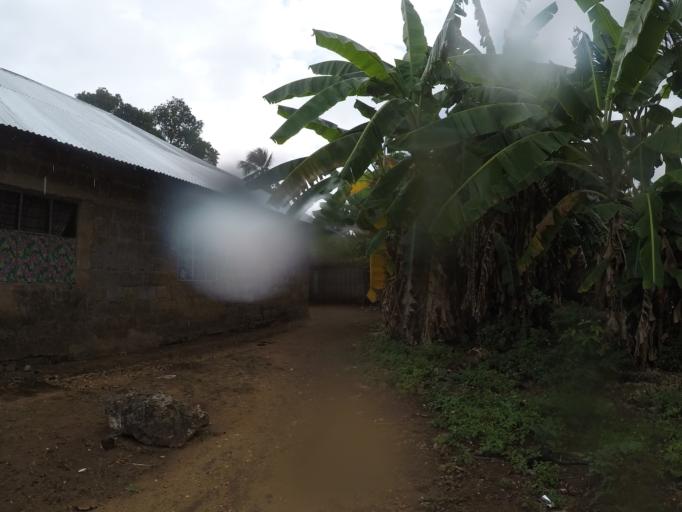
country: TZ
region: Zanzibar North
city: Mkokotoni
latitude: -5.9490
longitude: 39.1952
